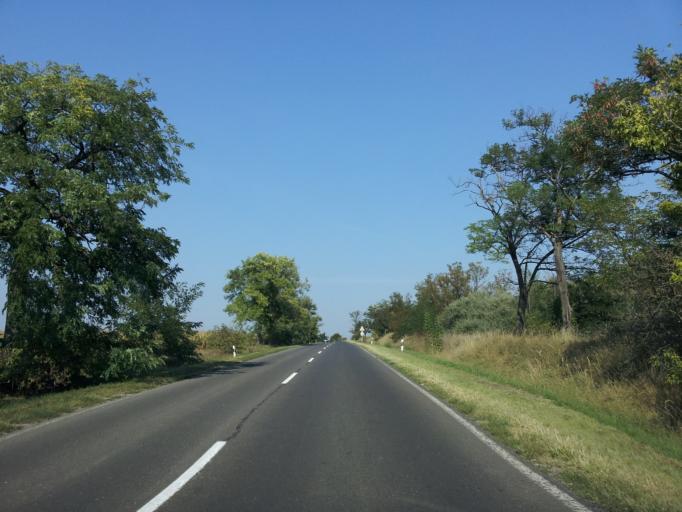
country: HU
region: Fejer
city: Lepseny
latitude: 47.0143
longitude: 18.2731
